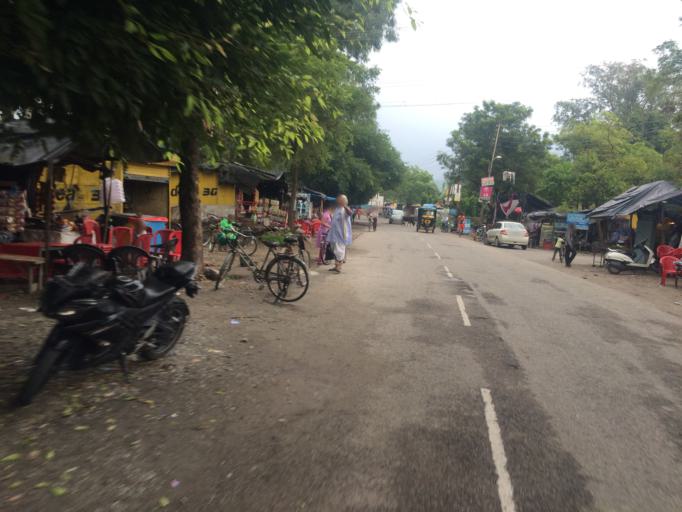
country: IN
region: Uttarakhand
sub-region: Dehradun
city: Birbhaddar
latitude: 30.0744
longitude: 78.2852
